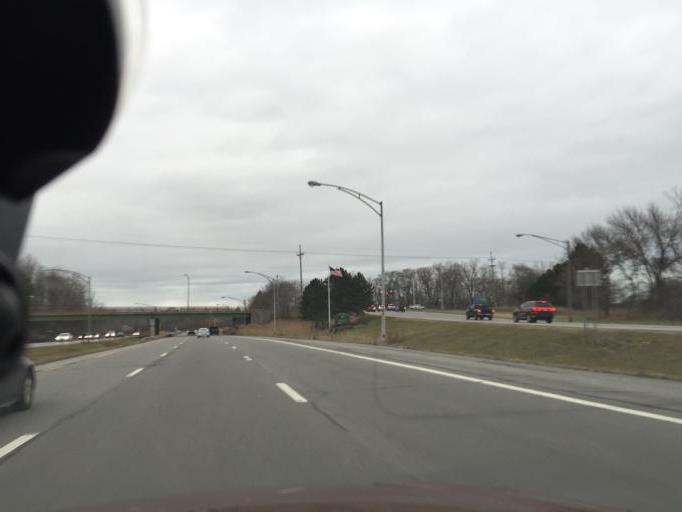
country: US
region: New York
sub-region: Monroe County
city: Greece
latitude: 43.1898
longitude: -77.6828
